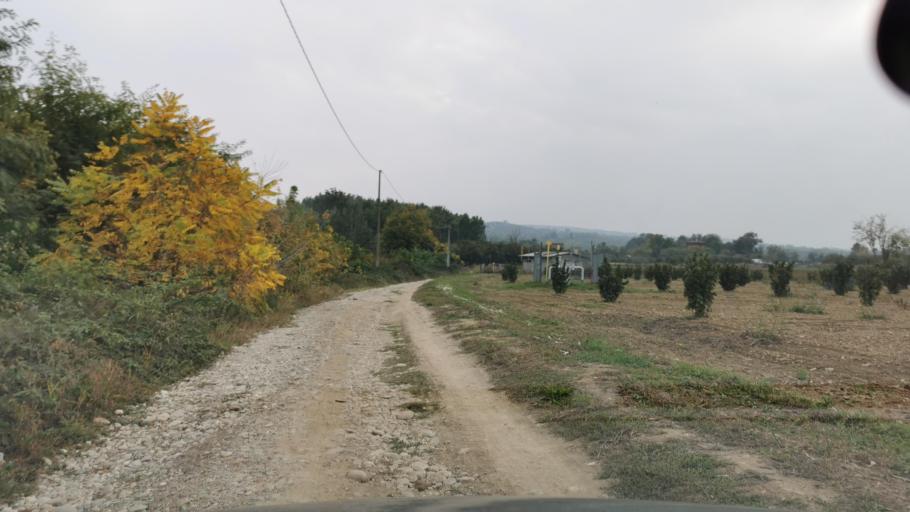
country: IT
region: Piedmont
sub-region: Provincia di Cuneo
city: Cinzano
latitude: 44.6893
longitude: 7.9129
